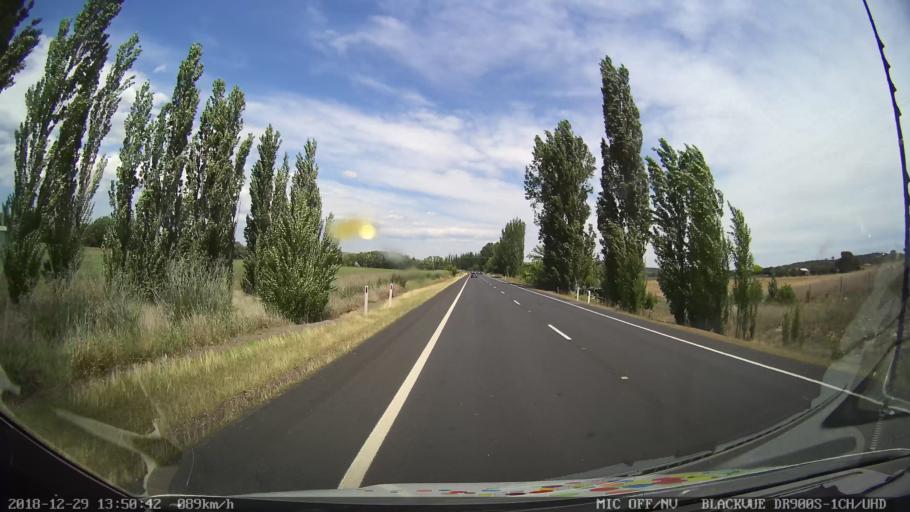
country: AU
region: New South Wales
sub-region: Cooma-Monaro
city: Cooma
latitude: -36.1713
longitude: 149.1539
